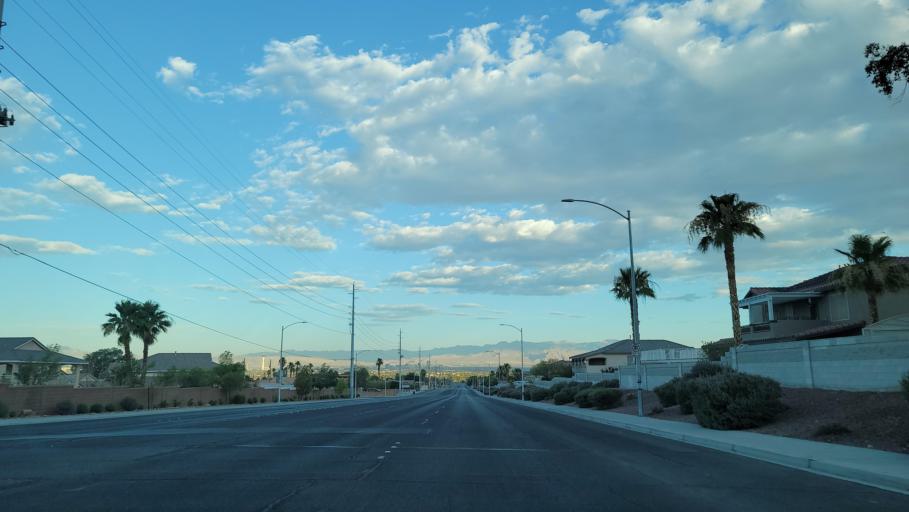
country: US
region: Nevada
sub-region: Clark County
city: Sunrise Manor
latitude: 36.1741
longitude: -115.0283
